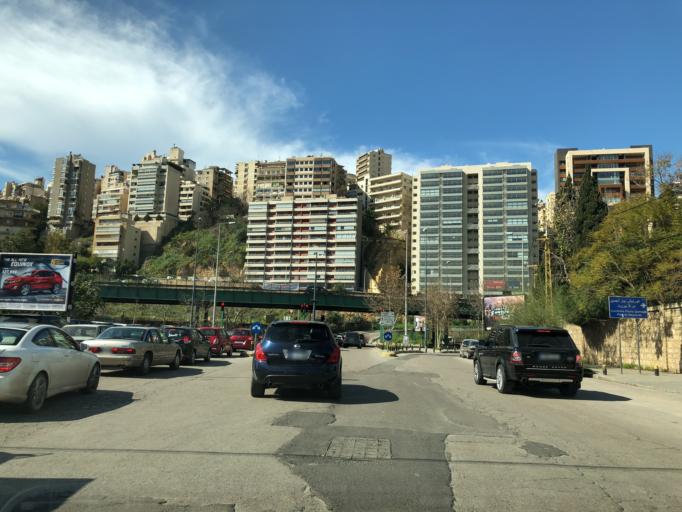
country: LB
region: Mont-Liban
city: Jdaidet el Matn
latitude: 33.8840
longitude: 35.5311
